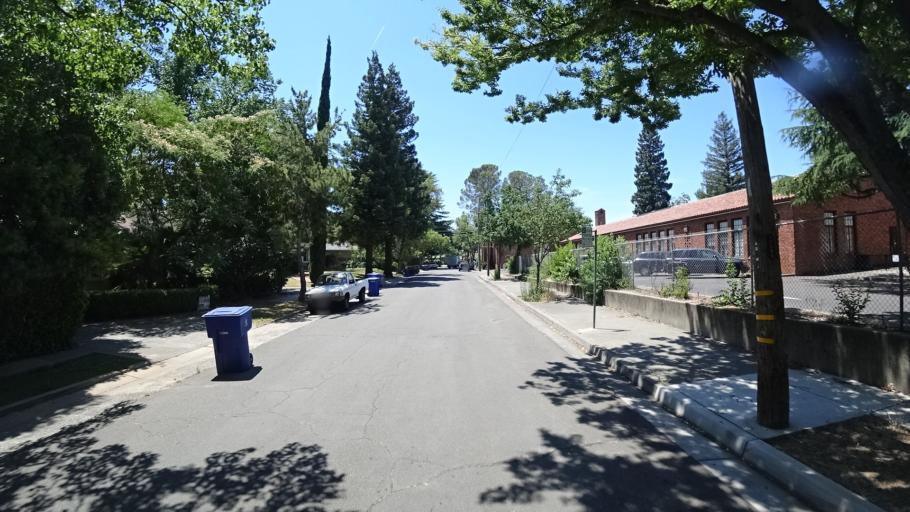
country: US
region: California
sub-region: Sacramento County
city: Sacramento
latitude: 38.5573
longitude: -121.4501
